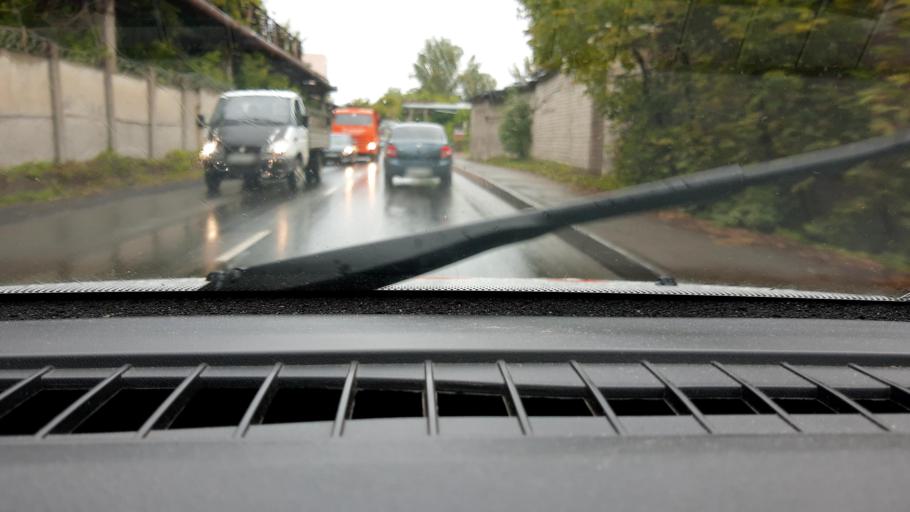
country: RU
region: Nizjnij Novgorod
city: Neklyudovo
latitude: 56.3539
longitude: 43.8832
